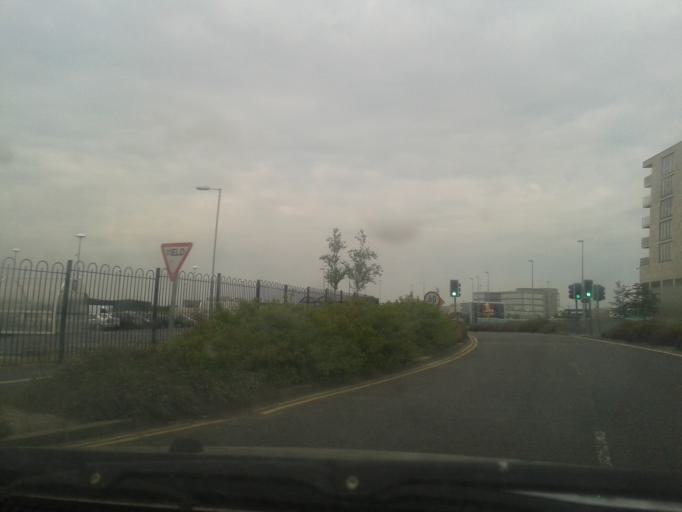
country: IE
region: Leinster
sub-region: Dublin City
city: Finglas
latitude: 53.4028
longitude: -6.3029
